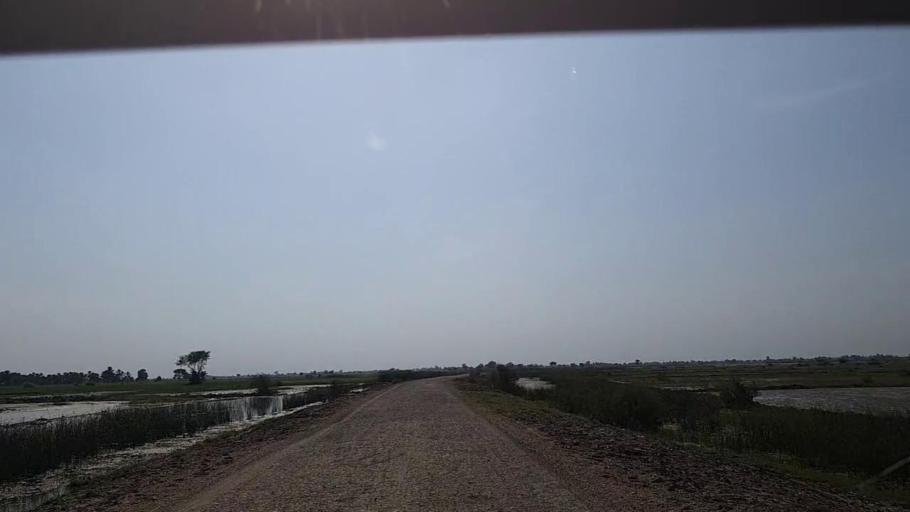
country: PK
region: Sindh
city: Khanpur
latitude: 27.8482
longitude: 69.3742
